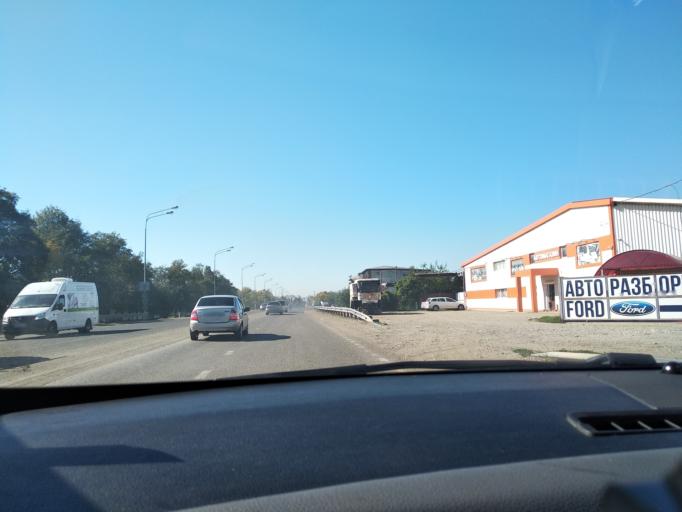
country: RU
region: Krasnodarskiy
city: Krasnodar
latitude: 45.1327
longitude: 39.0228
